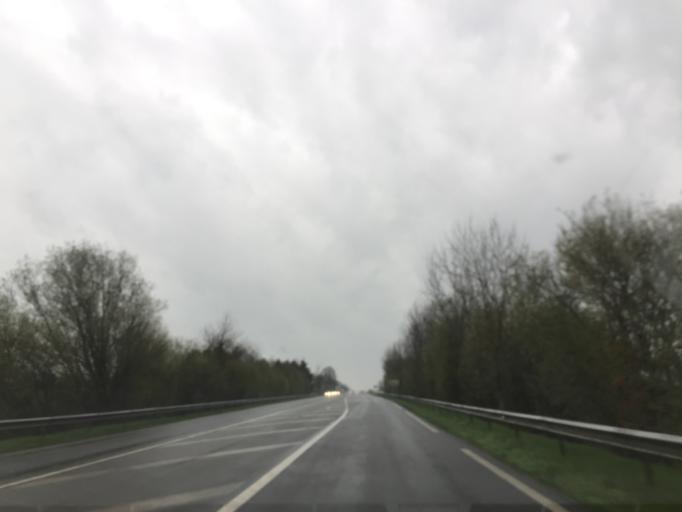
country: FR
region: Brittany
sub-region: Departement d'Ille-et-Vilaine
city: Luitre
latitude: 48.2880
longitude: -1.1549
